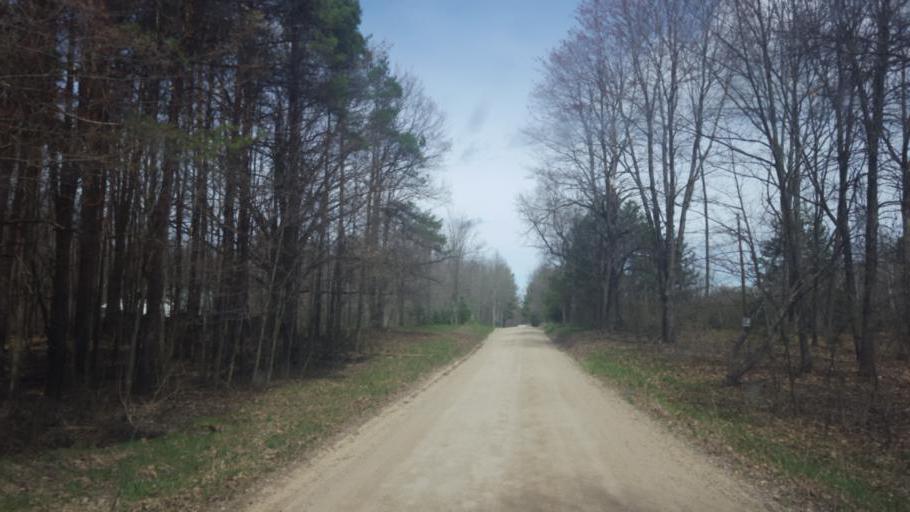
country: US
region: Michigan
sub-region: Isabella County
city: Lake Isabella
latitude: 43.5742
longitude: -84.9668
